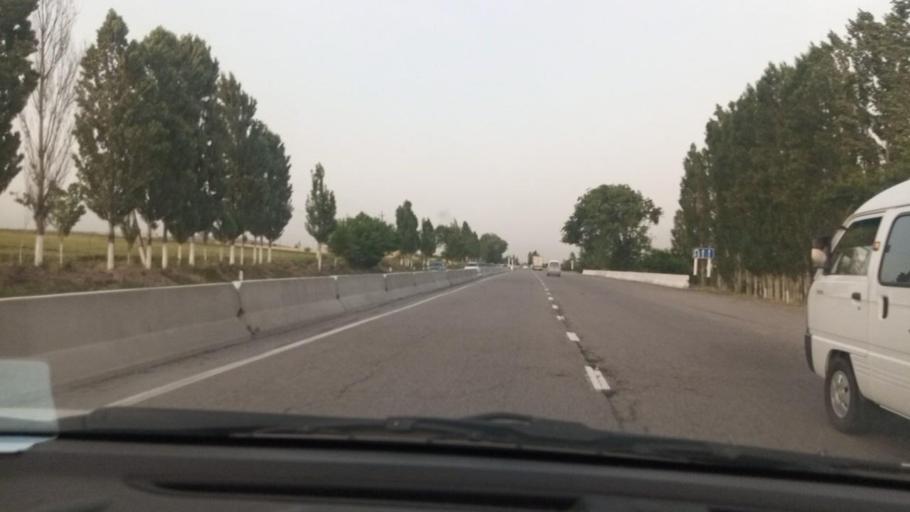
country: UZ
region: Toshkent
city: Angren
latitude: 40.9702
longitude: 69.9854
